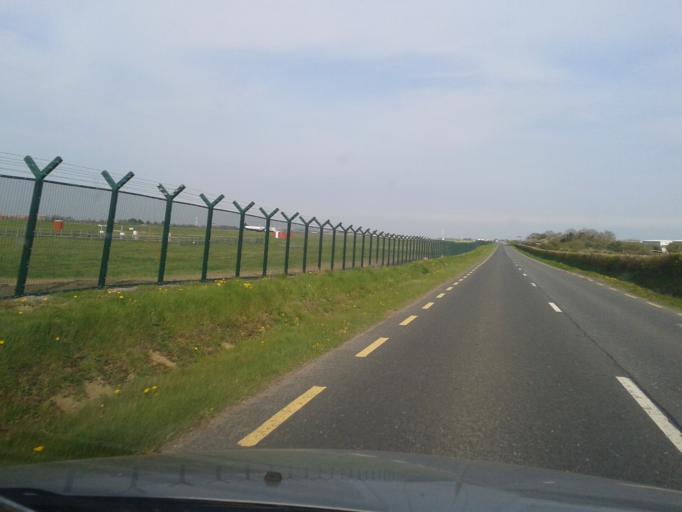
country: IE
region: Leinster
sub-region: Dublin City
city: Finglas
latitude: 53.4211
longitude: -6.2994
